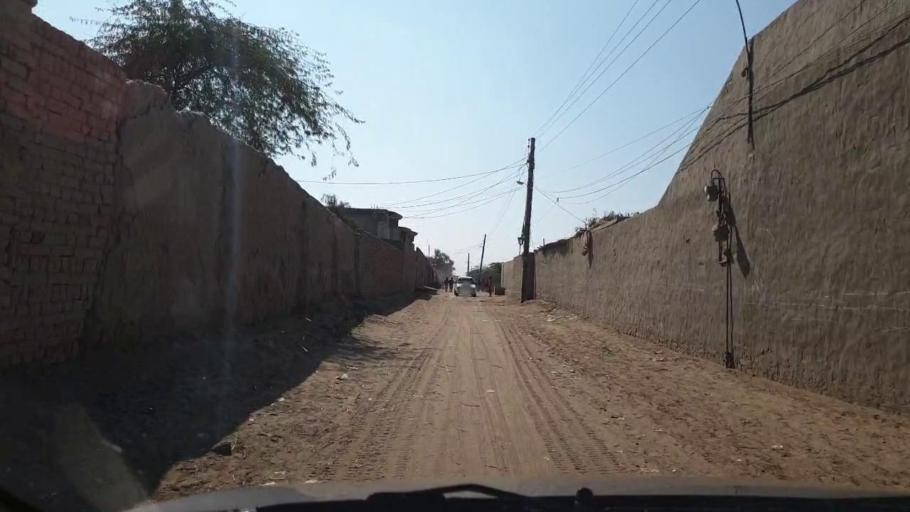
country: PK
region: Sindh
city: Sinjhoro
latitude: 25.9445
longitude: 68.7883
